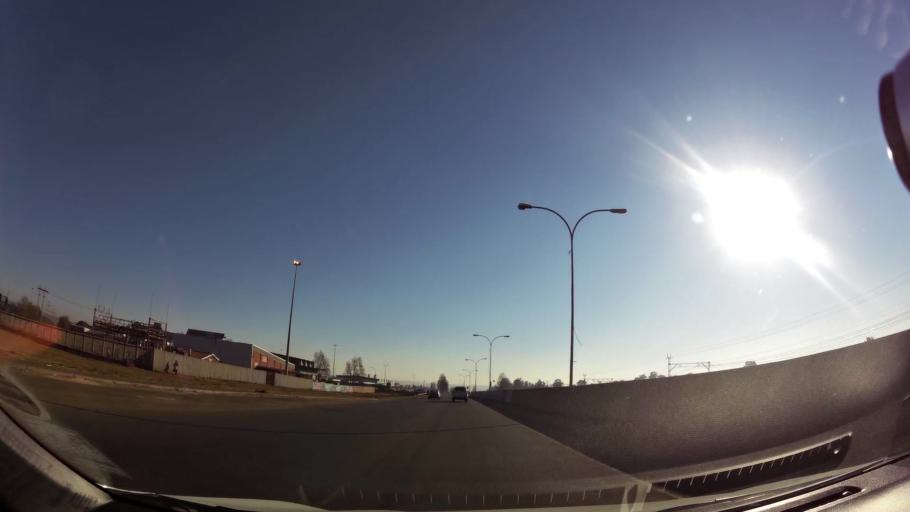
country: ZA
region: Gauteng
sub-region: Ekurhuleni Metropolitan Municipality
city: Germiston
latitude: -26.3239
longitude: 28.1390
